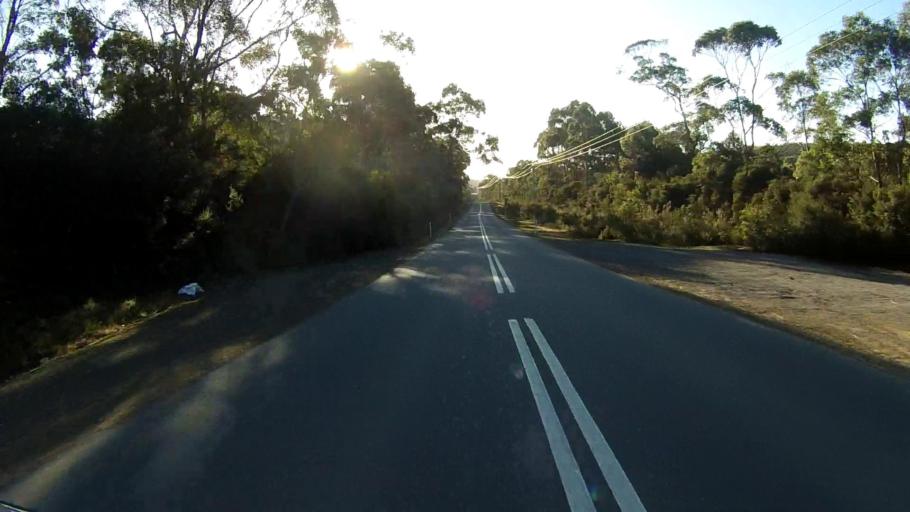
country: AU
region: Tasmania
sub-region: Clarence
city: Sandford
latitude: -43.0861
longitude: 147.8675
